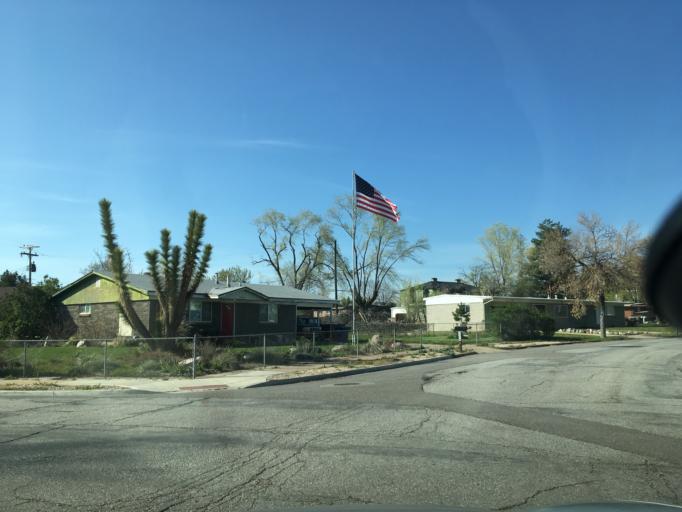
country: US
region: Utah
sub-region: Davis County
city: Layton
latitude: 41.0786
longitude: -111.9923
